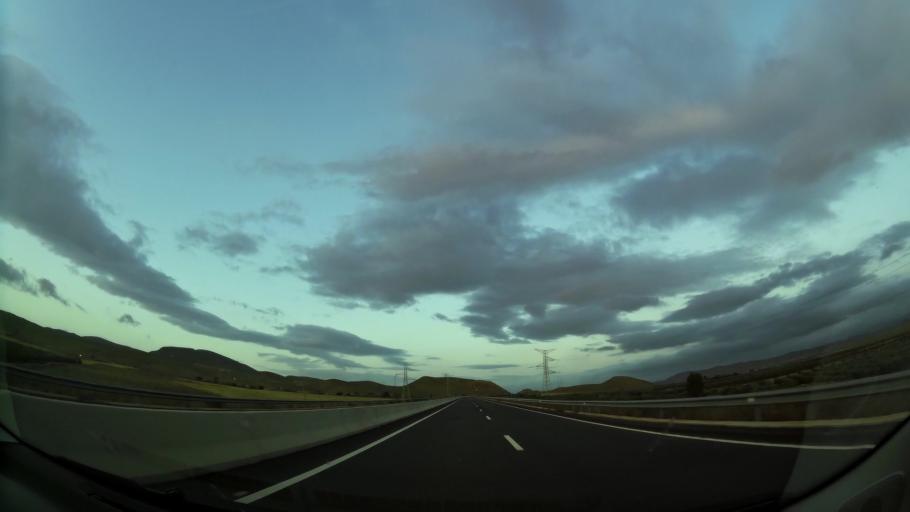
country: MA
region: Oriental
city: El Aioun
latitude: 34.5947
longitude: -2.6823
